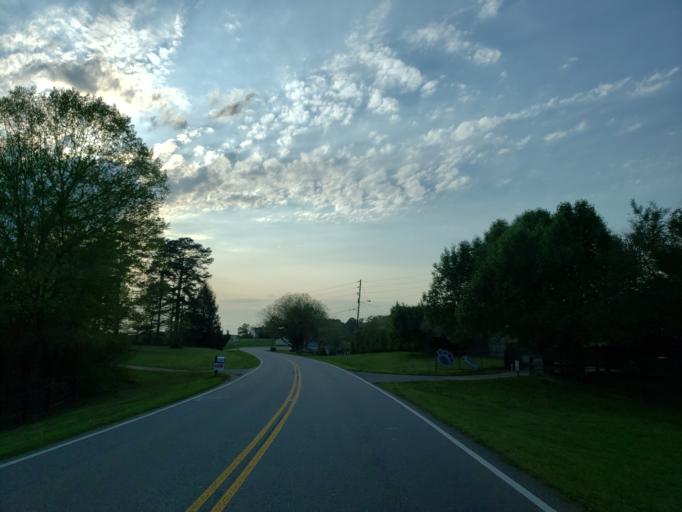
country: US
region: Georgia
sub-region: Cherokee County
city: Ball Ground
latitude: 34.2668
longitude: -84.3635
